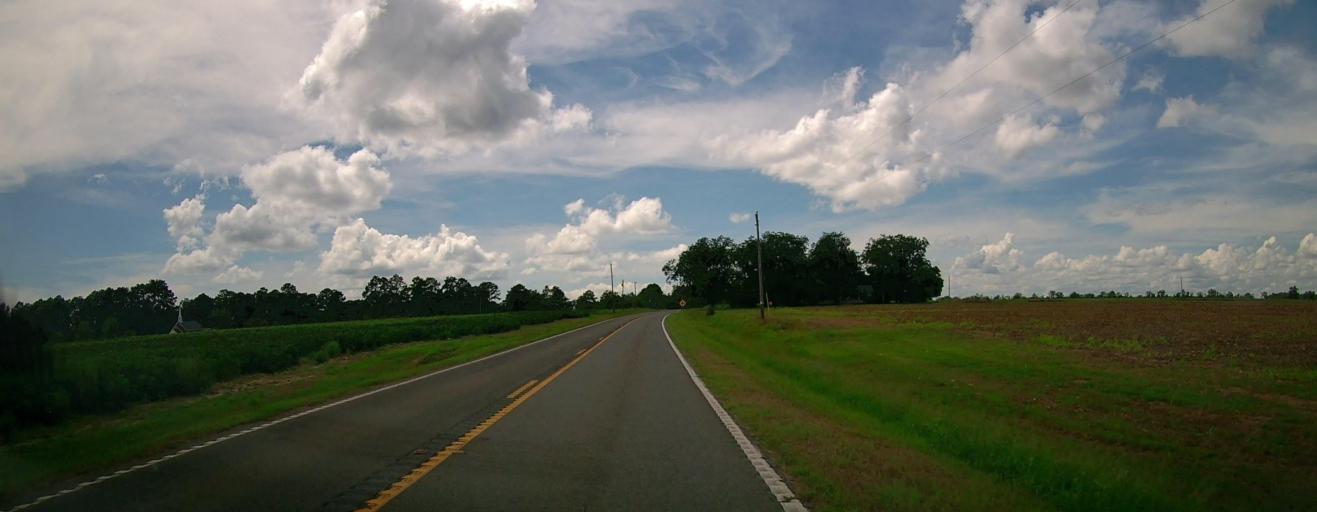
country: US
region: Georgia
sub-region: Taylor County
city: Reynolds
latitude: 32.4399
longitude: -84.1000
